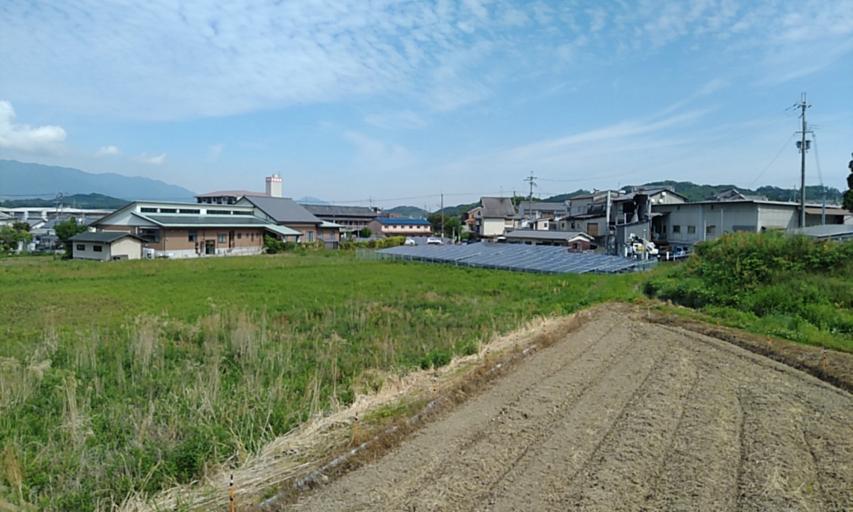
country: JP
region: Nara
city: Gose
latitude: 34.4428
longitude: 135.7784
